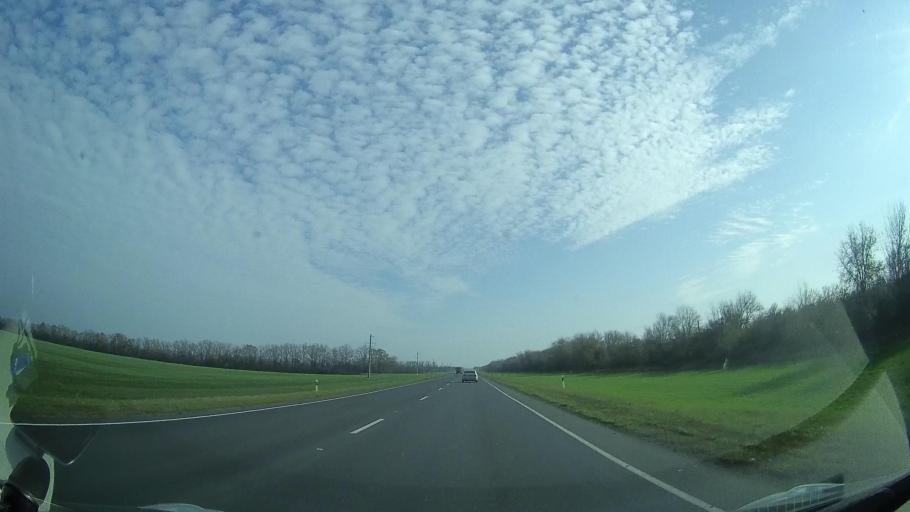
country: RU
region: Rostov
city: Gigant
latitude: 46.5283
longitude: 41.2006
